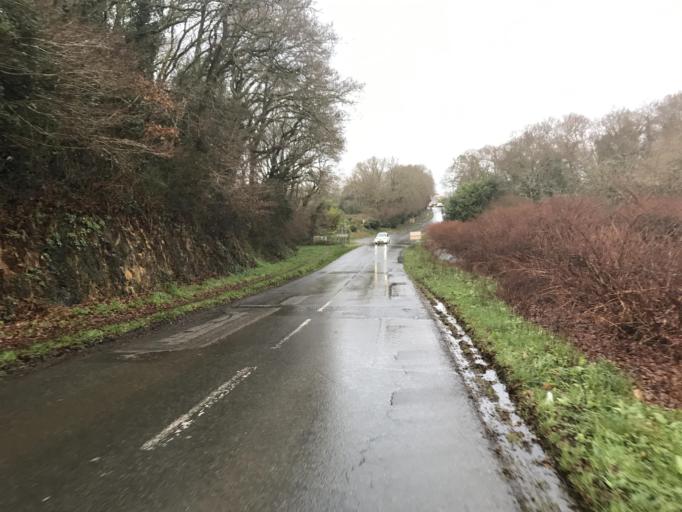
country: FR
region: Brittany
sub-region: Departement du Finistere
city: Loperhet
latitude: 48.3685
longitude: -4.3075
